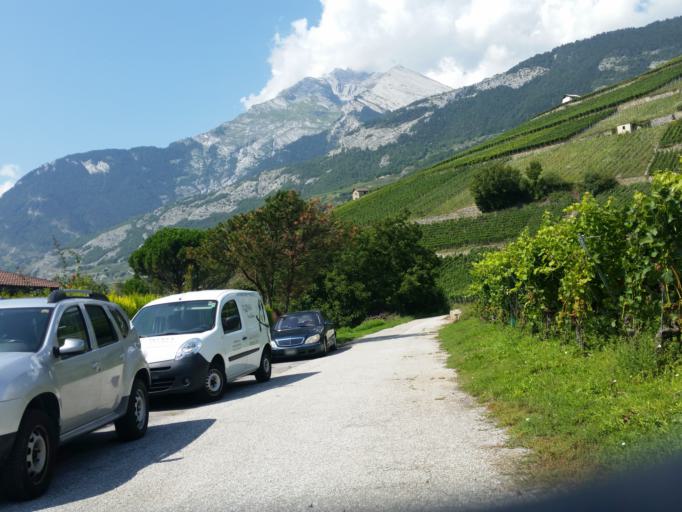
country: CH
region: Valais
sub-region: Conthey District
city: Vetroz
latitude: 46.2284
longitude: 7.2944
